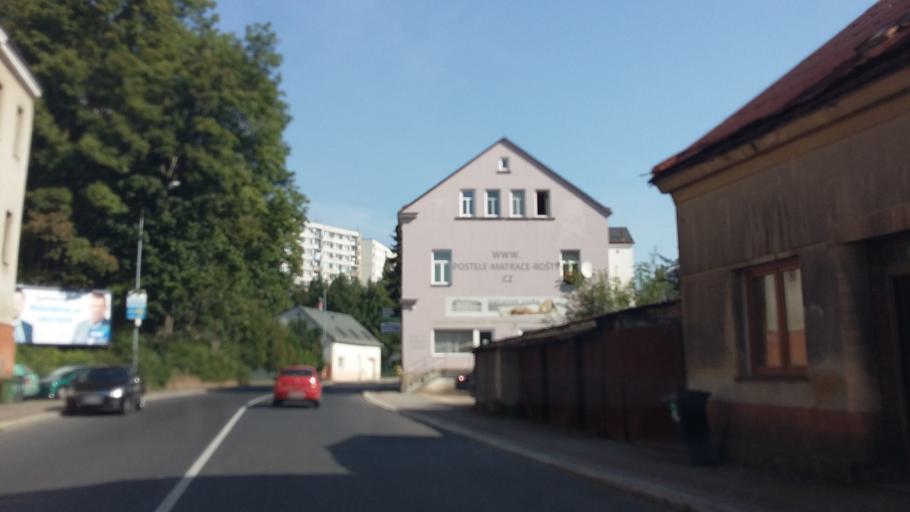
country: CZ
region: Liberecky
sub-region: Okres Jablonec nad Nisou
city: Jablonec nad Nisou
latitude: 50.7313
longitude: 15.1857
